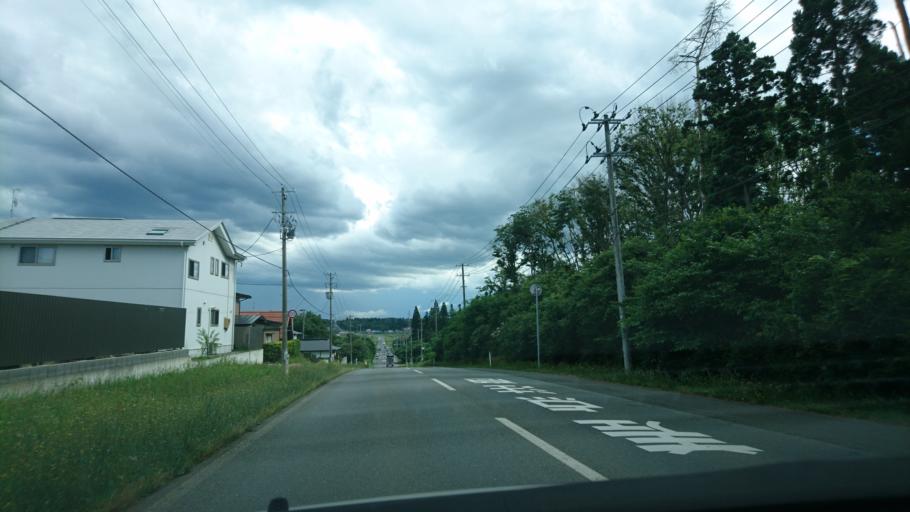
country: JP
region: Iwate
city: Kitakami
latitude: 39.3241
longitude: 141.1274
